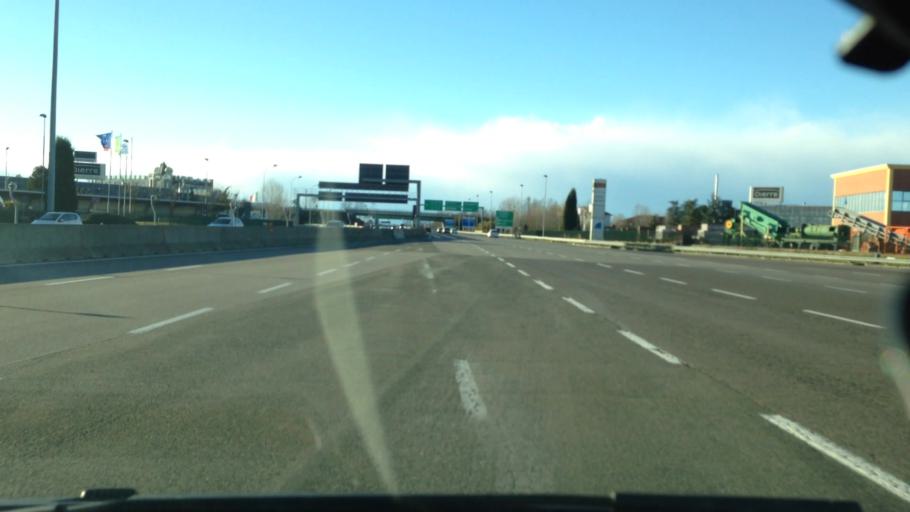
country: IT
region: Piedmont
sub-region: Provincia di Asti
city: Villanova d'Asti
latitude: 44.9532
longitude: 7.9222
